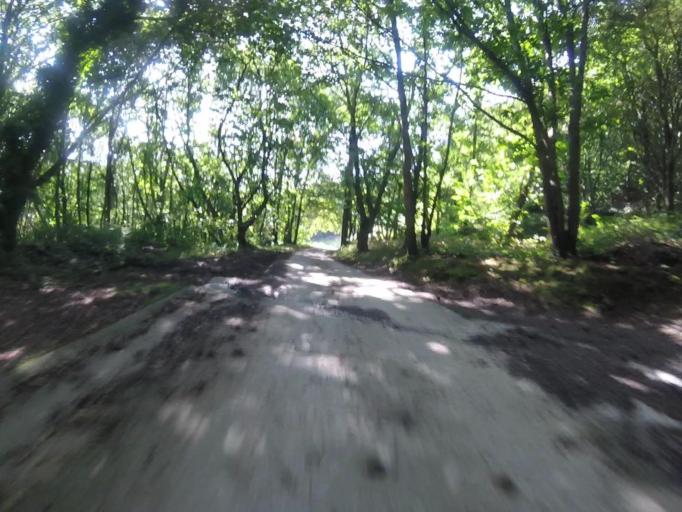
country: ES
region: Basque Country
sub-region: Provincia de Guipuzcoa
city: Irun
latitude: 43.3236
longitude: -1.7518
